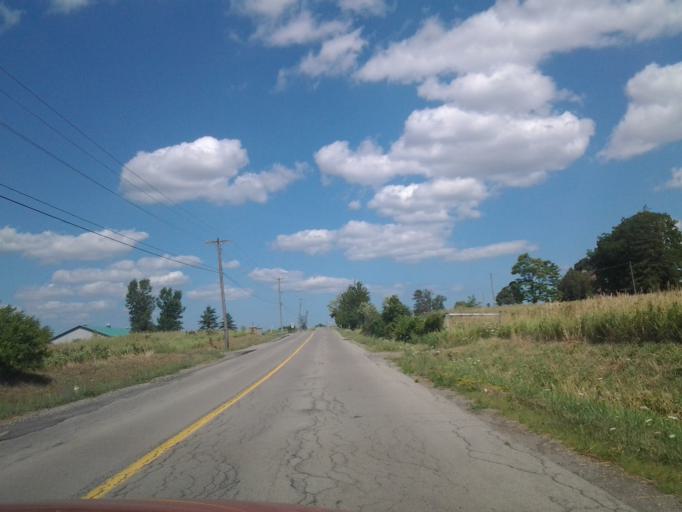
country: CA
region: Ontario
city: Ancaster
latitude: 43.2868
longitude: -79.9539
